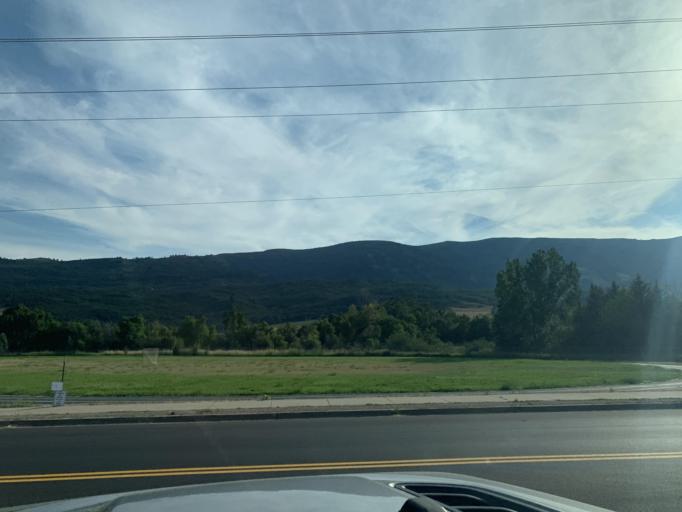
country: US
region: Utah
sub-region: Weber County
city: Wolf Creek
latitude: 41.3109
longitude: -111.8344
